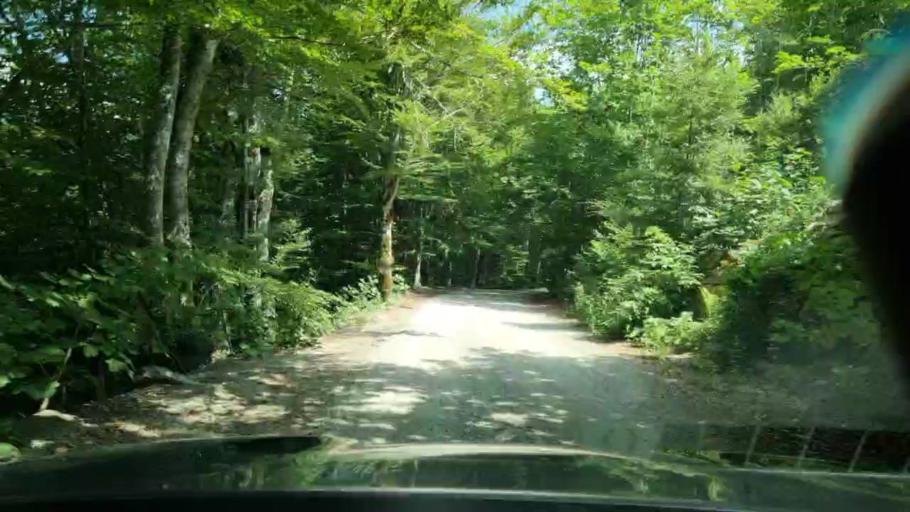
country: BA
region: Federation of Bosnia and Herzegovina
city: Bosansko Grahovo
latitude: 44.3000
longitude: 16.2631
